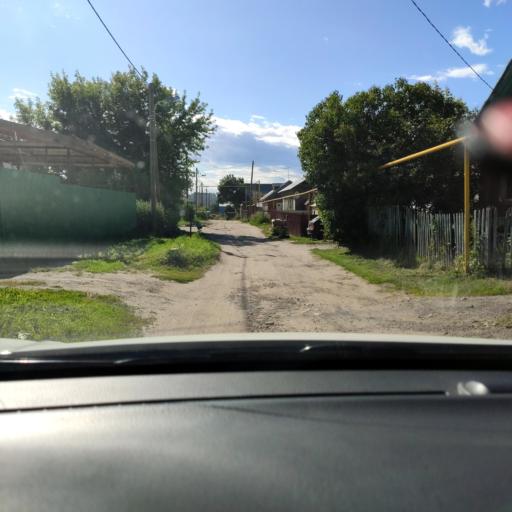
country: RU
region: Tatarstan
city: Vysokaya Gora
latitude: 55.7992
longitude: 49.2677
